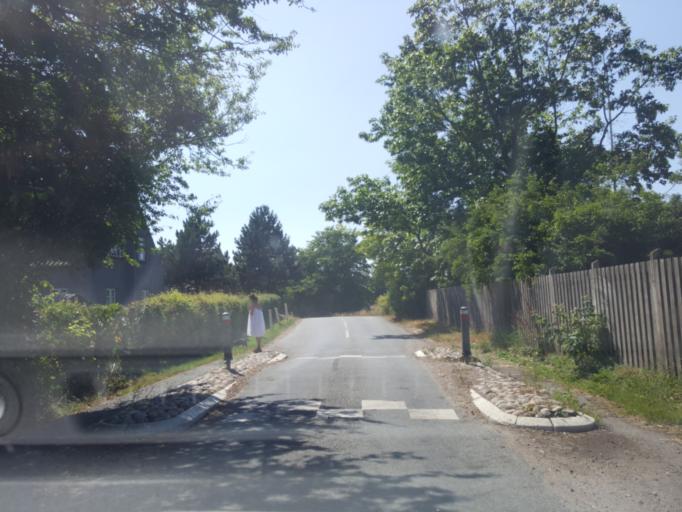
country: DK
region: Capital Region
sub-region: Fredensborg Kommune
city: Kokkedal
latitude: 55.9195
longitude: 12.4404
